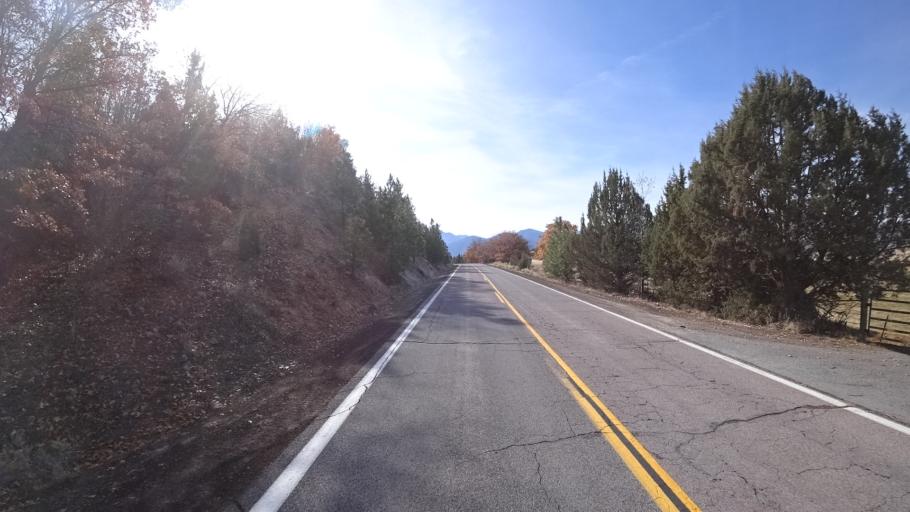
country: US
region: California
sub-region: Siskiyou County
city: Weed
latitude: 41.4761
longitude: -122.4118
